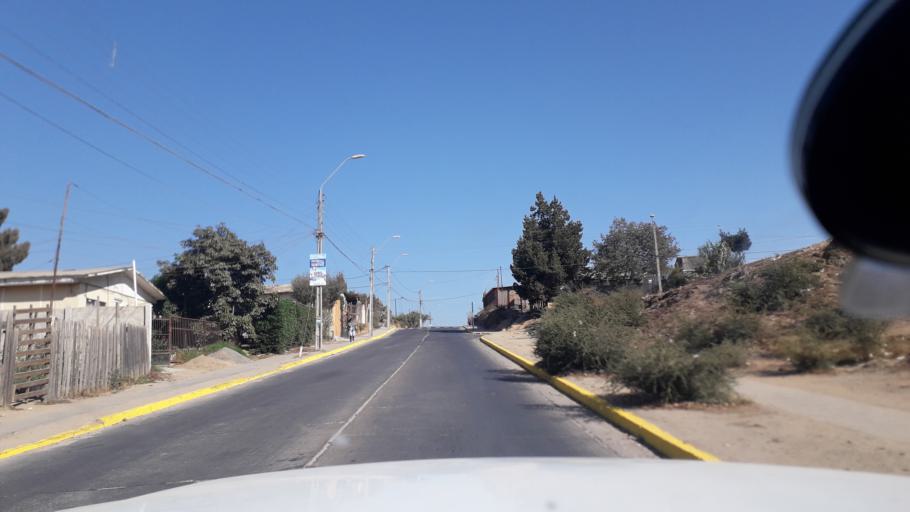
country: CL
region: Valparaiso
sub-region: Provincia de Marga Marga
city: Villa Alemana
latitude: -33.0637
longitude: -71.4028
